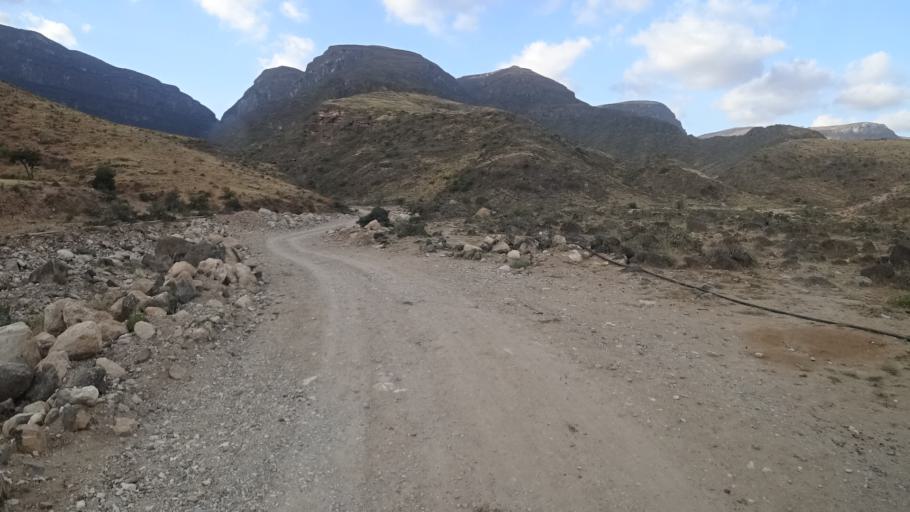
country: OM
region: Zufar
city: Salalah
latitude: 16.9953
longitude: 53.8462
